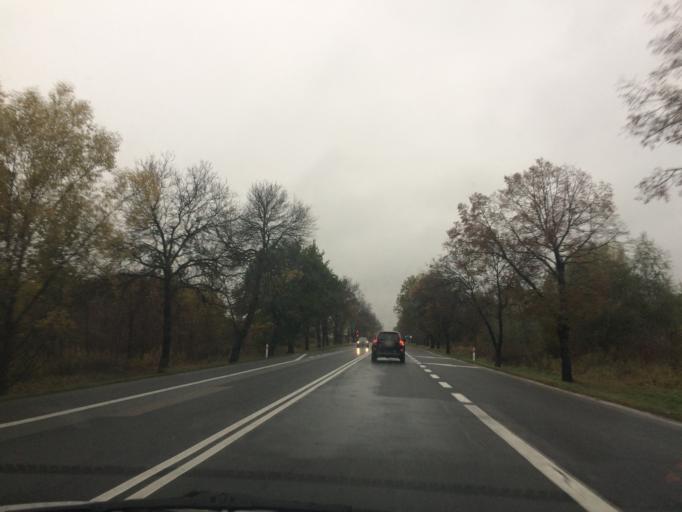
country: PL
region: Masovian Voivodeship
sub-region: Powiat otwocki
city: Celestynow
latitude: 52.1157
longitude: 21.3729
